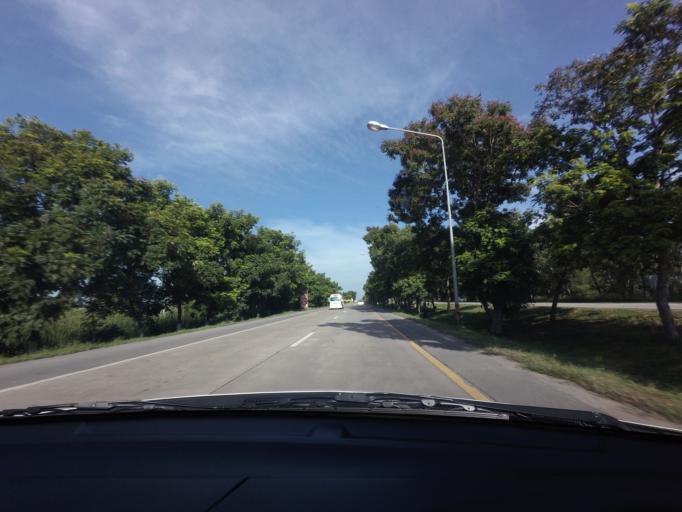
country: TH
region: Suphan Buri
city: Bang Pla Ma
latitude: 14.3317
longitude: 100.2085
